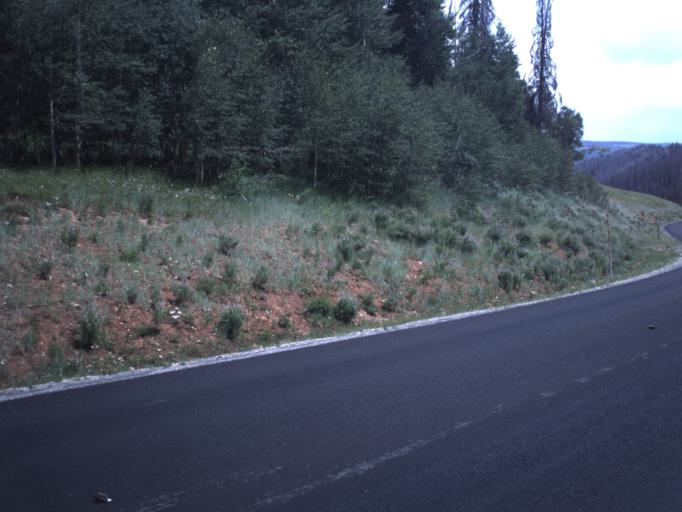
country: US
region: Utah
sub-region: Summit County
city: Francis
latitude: 40.4865
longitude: -111.0062
